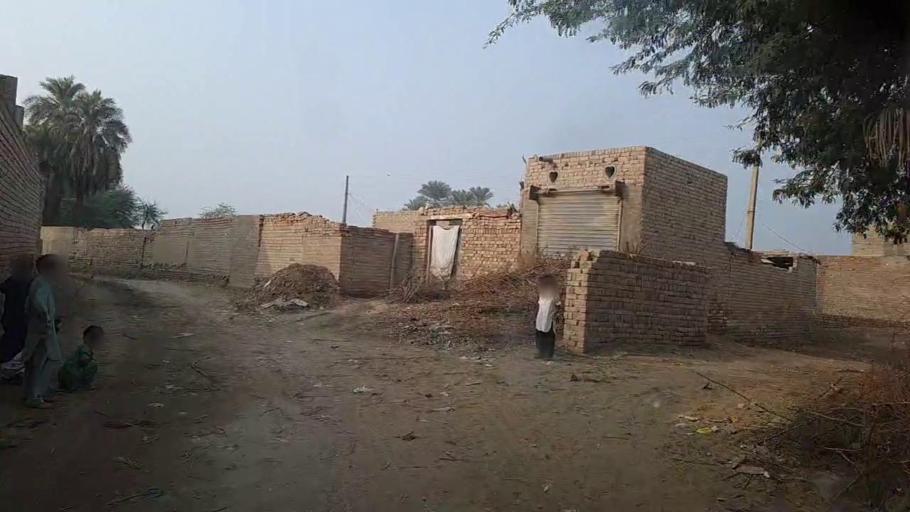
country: PK
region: Sindh
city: Bozdar
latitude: 27.1691
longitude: 68.6585
